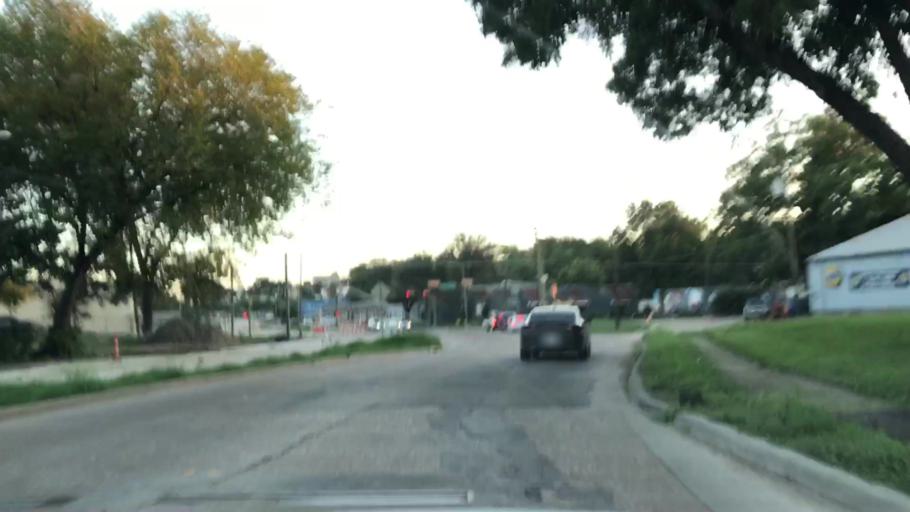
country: US
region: Texas
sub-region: Dallas County
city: Dallas
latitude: 32.7739
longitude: -96.8358
